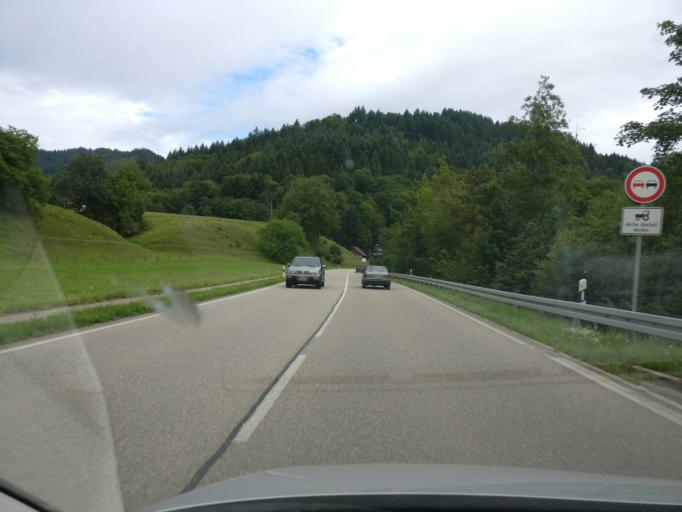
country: DE
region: Baden-Wuerttemberg
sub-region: Freiburg Region
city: Lautenbach
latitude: 48.5094
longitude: 8.1334
